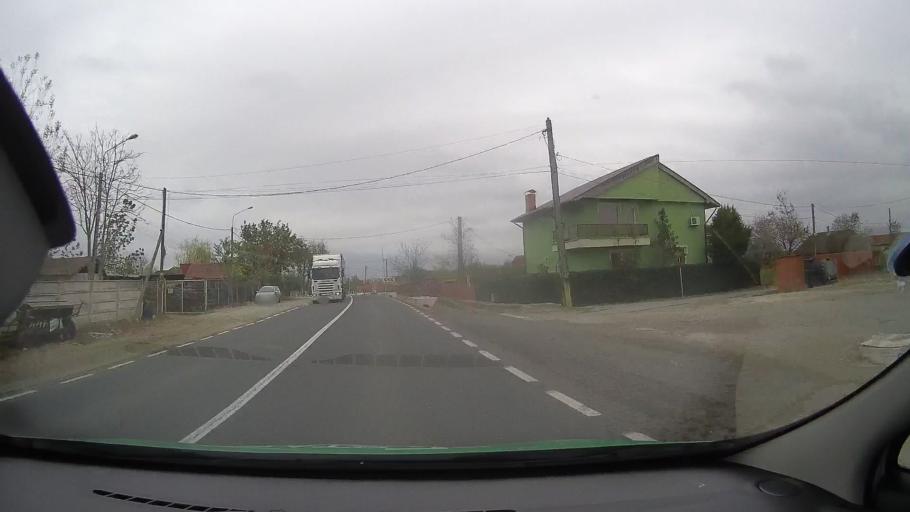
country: RO
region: Constanta
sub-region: Comuna Mihail Kogalniceanu
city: Mihail Kogalniceanu
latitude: 44.3679
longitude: 28.4529
